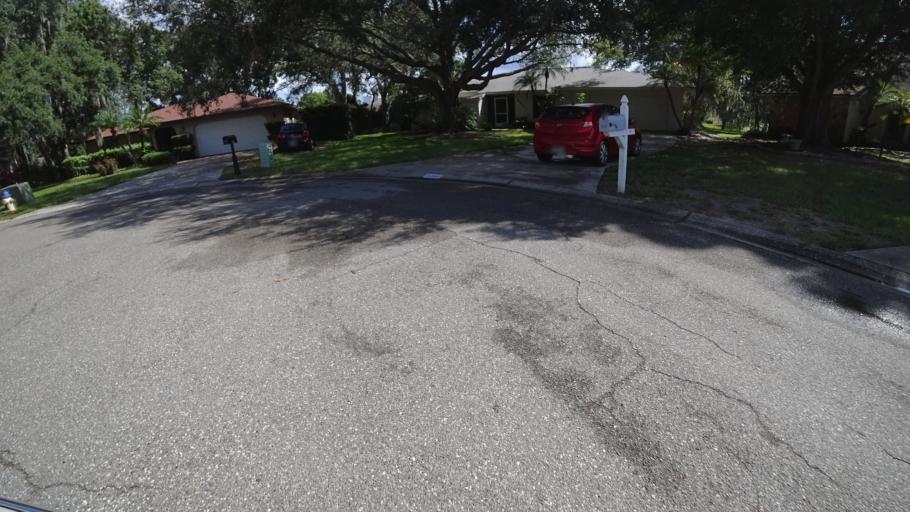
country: US
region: Florida
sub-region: Sarasota County
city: Desoto Lakes
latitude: 27.3920
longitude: -82.4994
